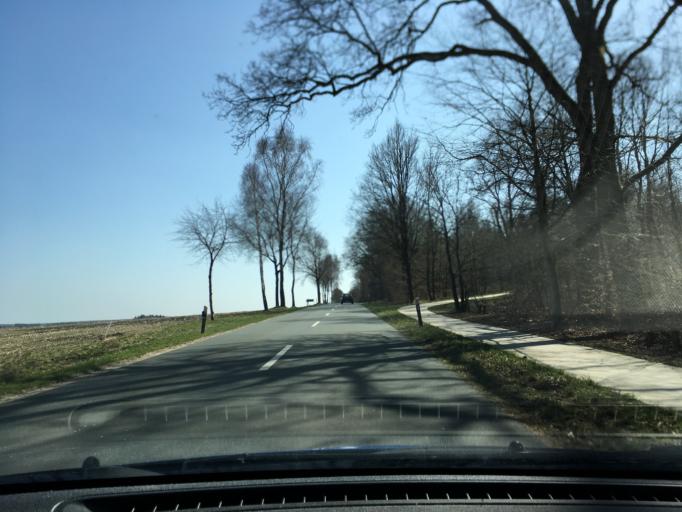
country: DE
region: Lower Saxony
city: Eimke
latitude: 52.9860
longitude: 10.3074
